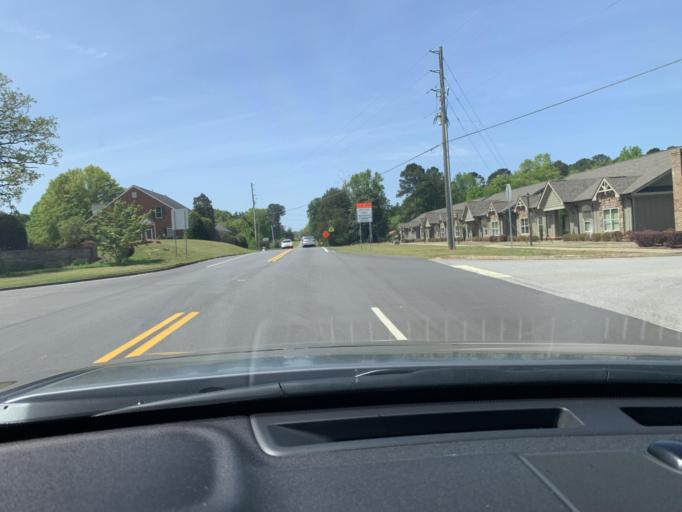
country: US
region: Georgia
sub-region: Oconee County
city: Watkinsville
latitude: 33.8792
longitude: -83.4339
